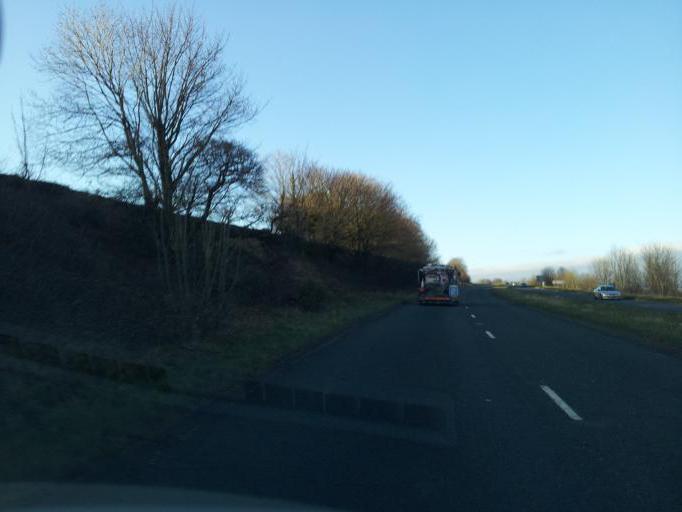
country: GB
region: England
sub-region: Cumbria
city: Kendal
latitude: 54.3108
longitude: -2.7642
